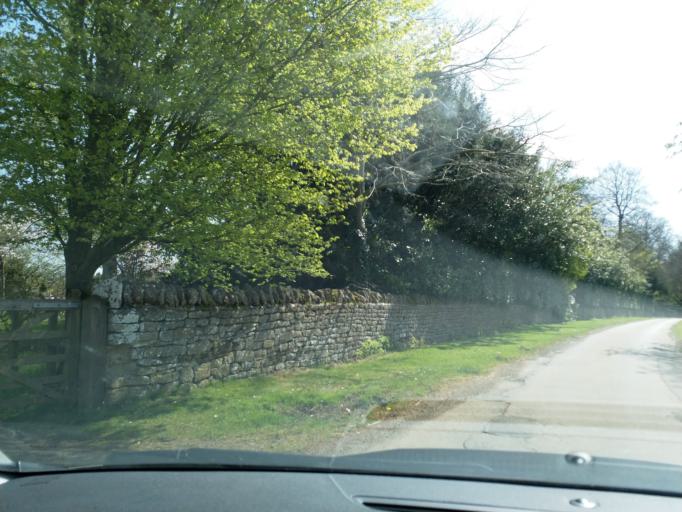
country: GB
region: England
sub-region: Oxfordshire
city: Adderbury
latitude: 52.0748
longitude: -1.2416
